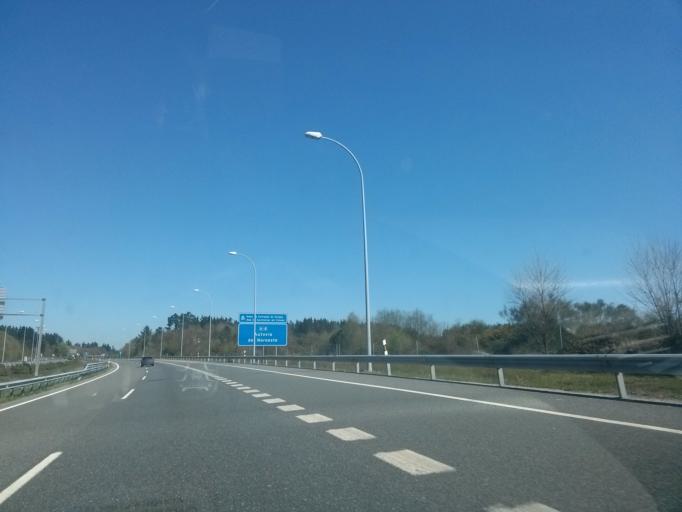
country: ES
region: Galicia
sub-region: Provincia de Lugo
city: Lugo
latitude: 43.0182
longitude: -7.5198
